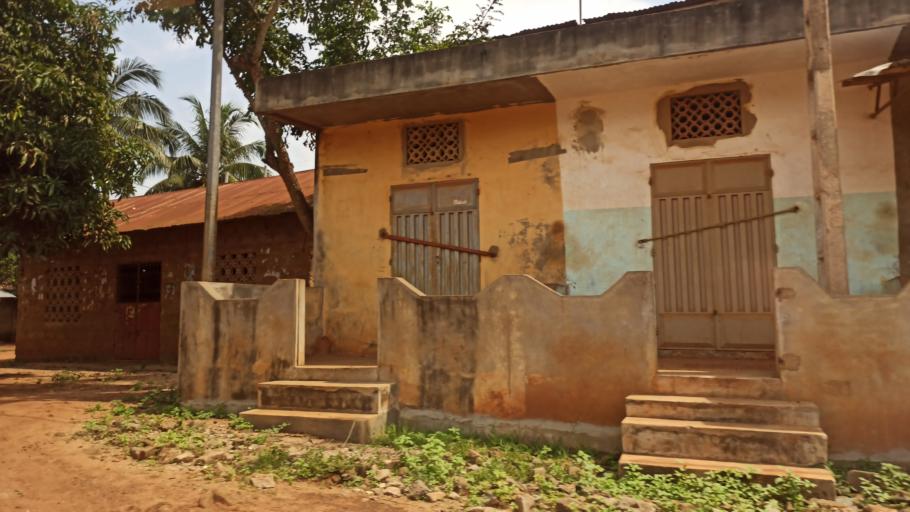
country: BJ
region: Queme
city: Porto-Novo
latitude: 6.4830
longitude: 2.5918
